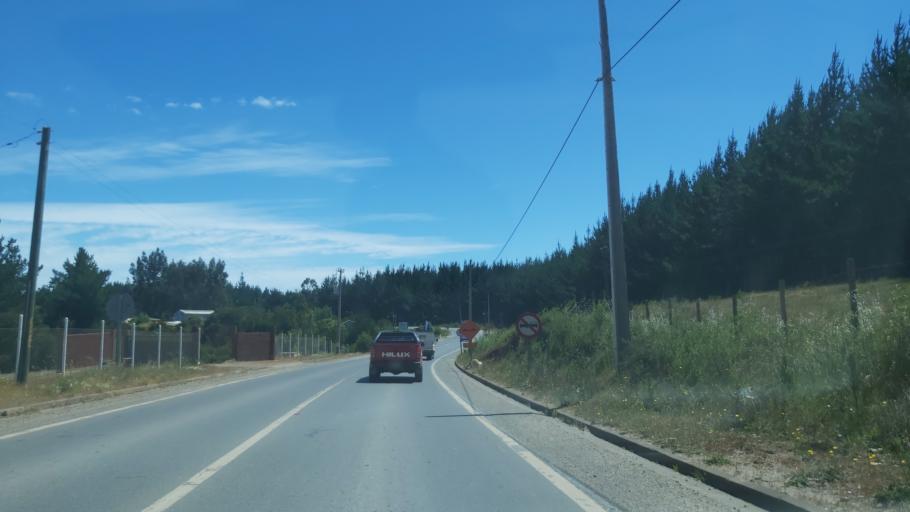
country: CL
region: Maule
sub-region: Provincia de Talca
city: Constitucion
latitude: -35.3981
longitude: -72.4334
